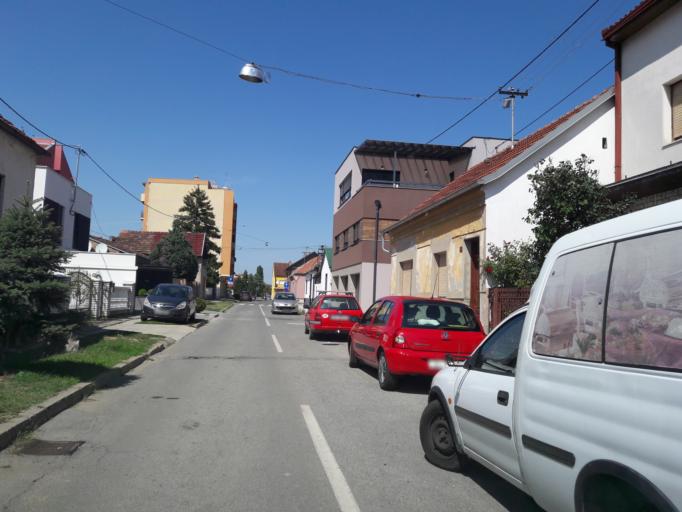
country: HR
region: Osjecko-Baranjska
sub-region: Grad Osijek
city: Osijek
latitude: 45.5565
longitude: 18.6547
